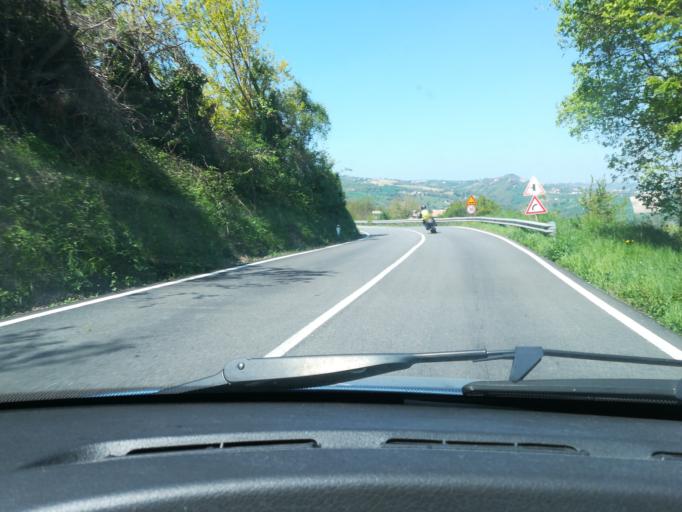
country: IT
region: The Marches
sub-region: Provincia di Macerata
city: Cingoli
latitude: 43.3886
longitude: 13.2049
